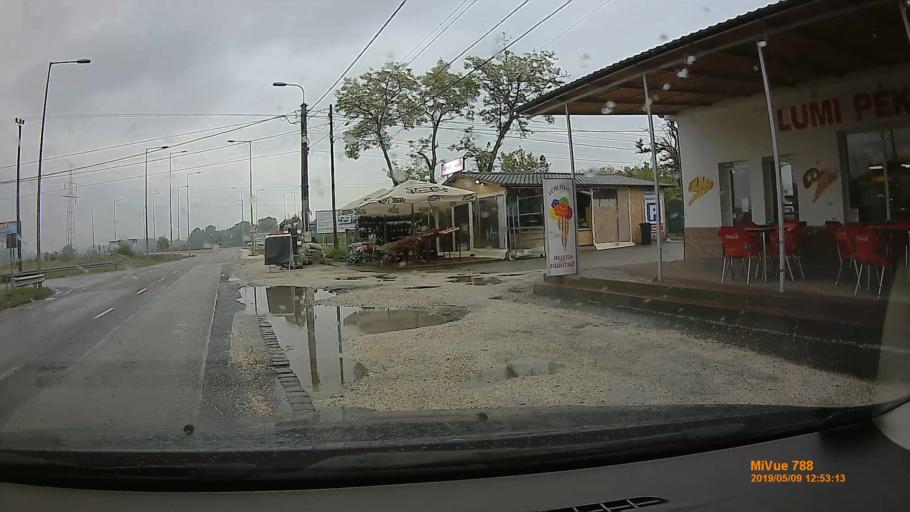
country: HU
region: Budapest
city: Budapest XVI. keruelet
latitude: 47.5421
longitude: 19.1712
